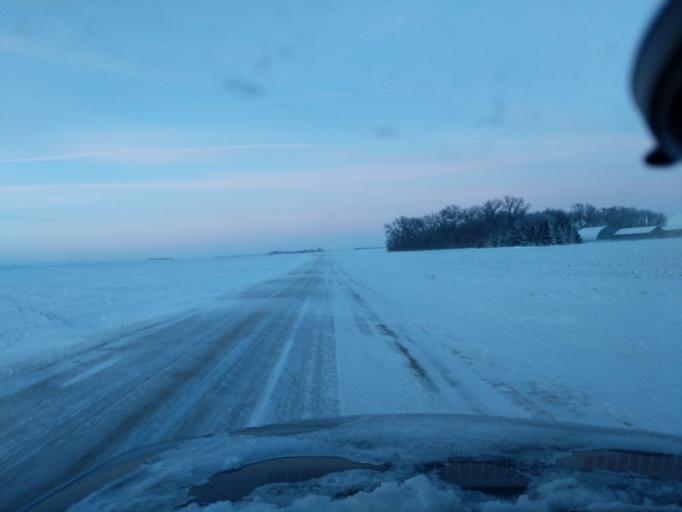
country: US
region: Minnesota
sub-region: Renville County
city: Renville
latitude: 44.7272
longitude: -95.3573
